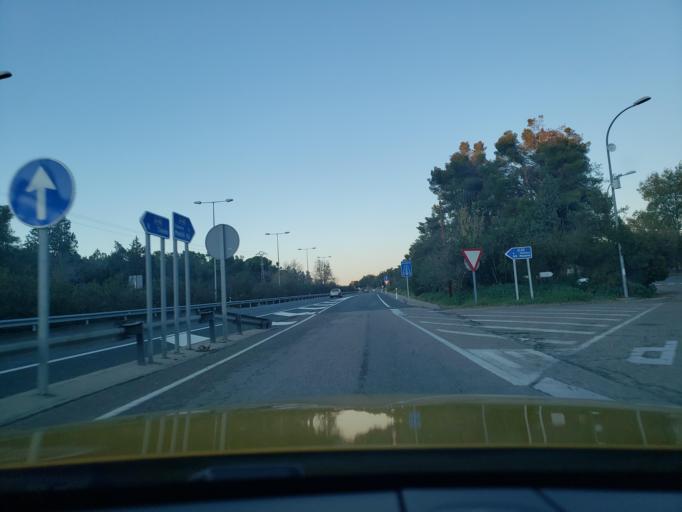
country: ES
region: Castille-La Mancha
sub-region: Province of Toledo
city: Bargas
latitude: 39.9214
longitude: -4.0046
